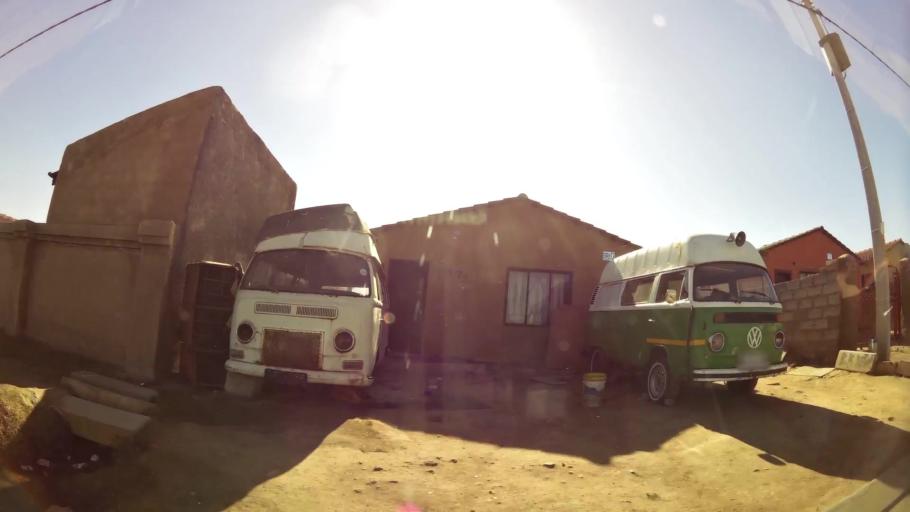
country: ZA
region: Gauteng
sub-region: Ekurhuleni Metropolitan Municipality
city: Tembisa
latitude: -26.0326
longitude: 28.2236
